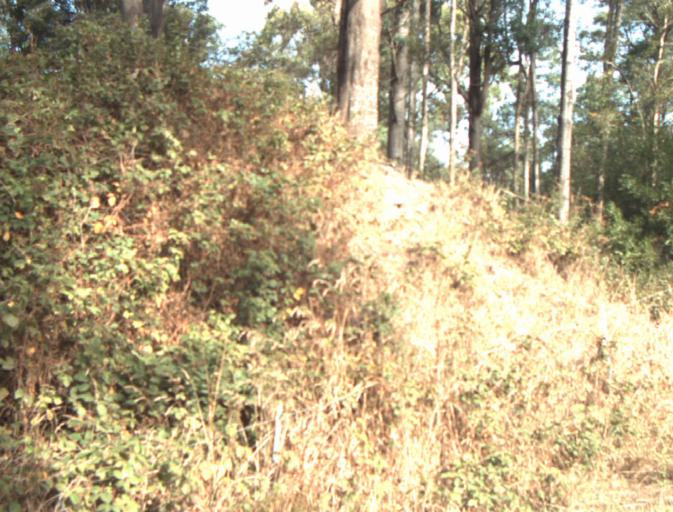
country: AU
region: Tasmania
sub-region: Launceston
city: Mayfield
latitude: -41.1896
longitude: 147.2124
